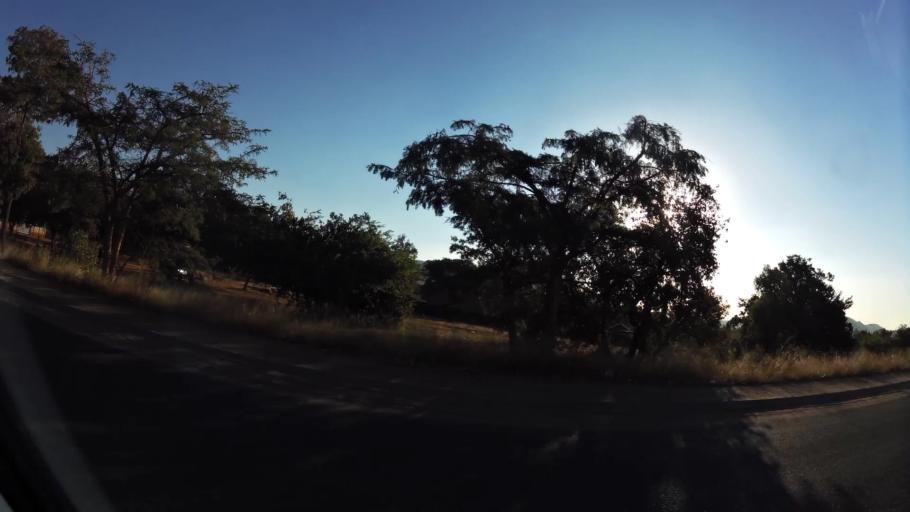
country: ZA
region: North-West
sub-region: Bojanala Platinum District Municipality
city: Rustenburg
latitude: -25.6898
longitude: 27.2162
